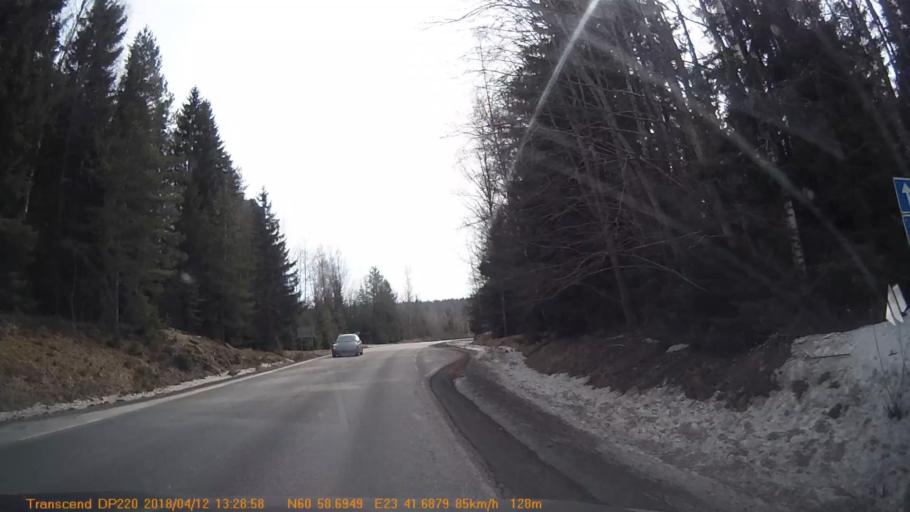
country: FI
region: Pirkanmaa
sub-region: Etelae-Pirkanmaa
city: Kylmaekoski
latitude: 60.9780
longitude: 23.6950
